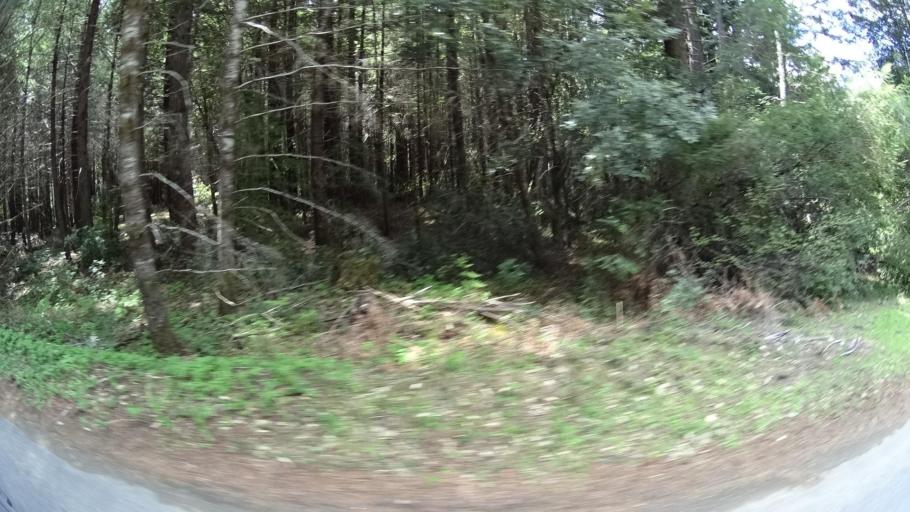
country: US
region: California
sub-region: Humboldt County
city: Redway
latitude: 40.0328
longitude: -123.9537
